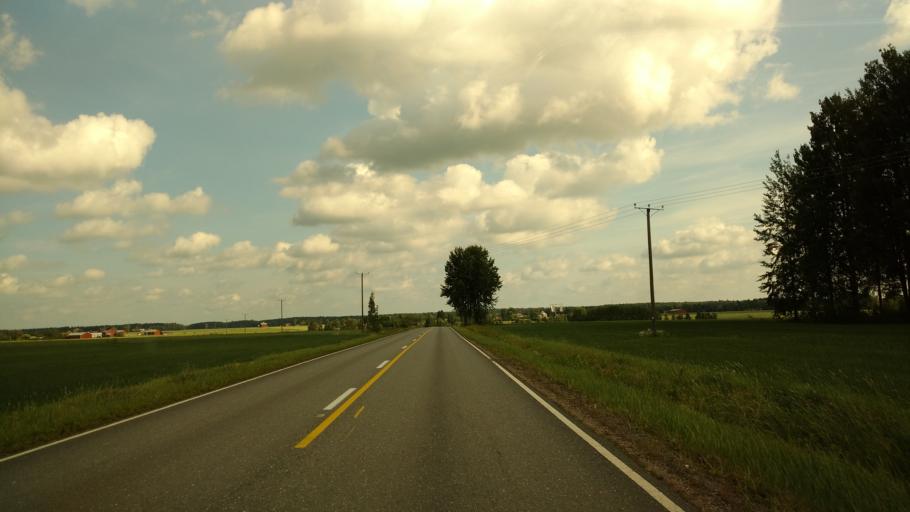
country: FI
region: Varsinais-Suomi
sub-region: Loimaa
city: Koski Tl
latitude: 60.6343
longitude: 23.1058
